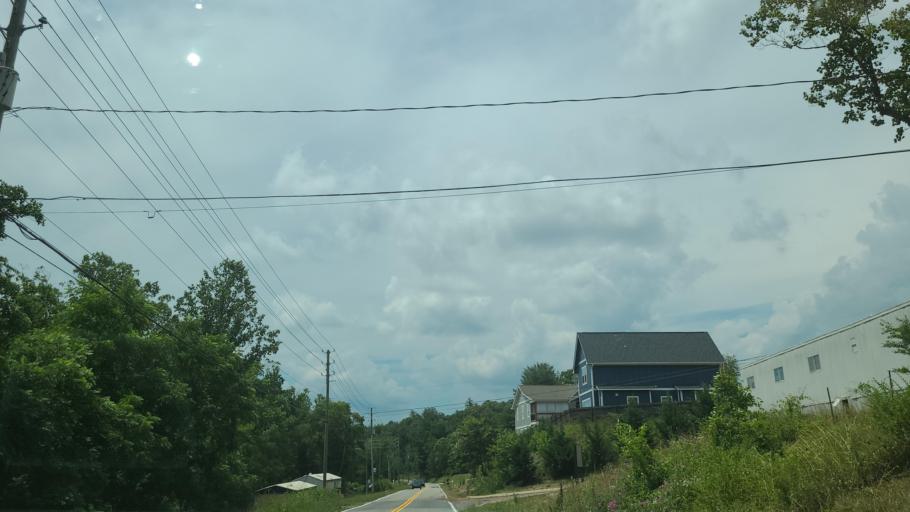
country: US
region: North Carolina
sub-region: Buncombe County
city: Avery Creek
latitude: 35.4864
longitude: -82.5719
